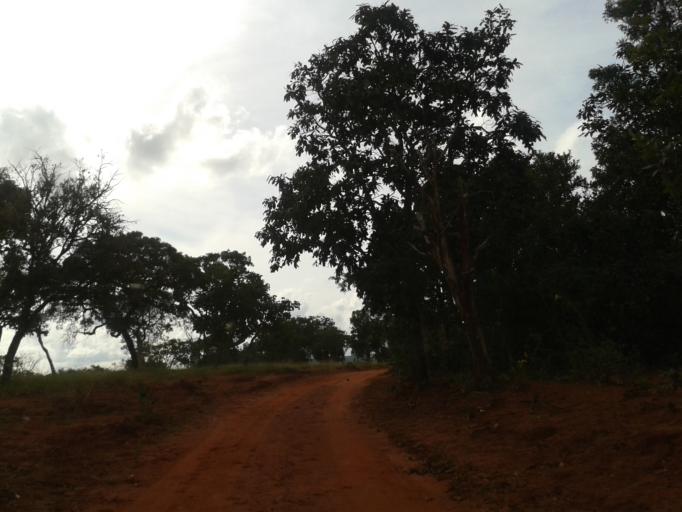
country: BR
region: Minas Gerais
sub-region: Campina Verde
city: Campina Verde
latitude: -19.4395
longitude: -49.6180
